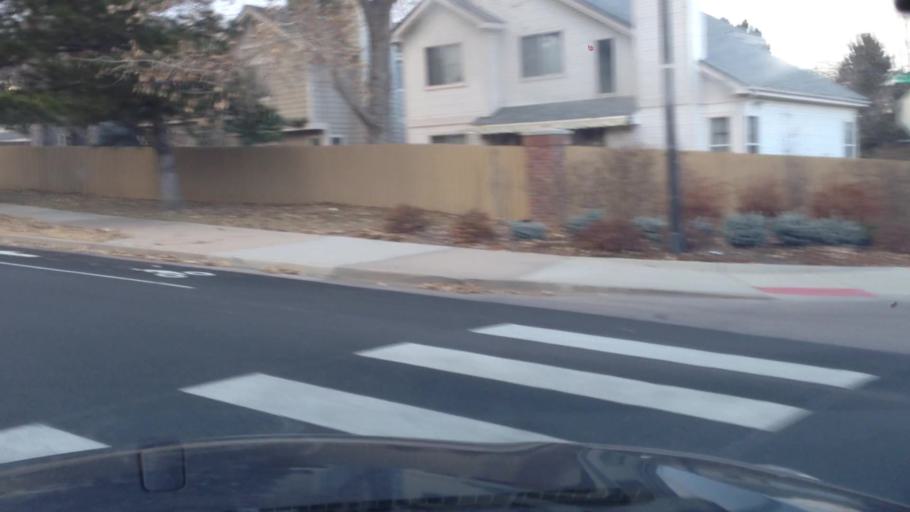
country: US
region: Colorado
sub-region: Douglas County
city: Stonegate
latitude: 39.5182
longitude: -104.7909
